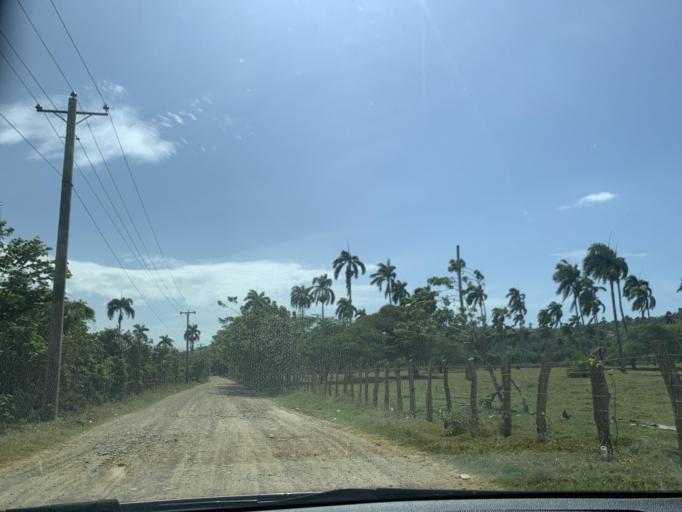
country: DO
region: Puerto Plata
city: Luperon
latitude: 19.8900
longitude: -70.8808
